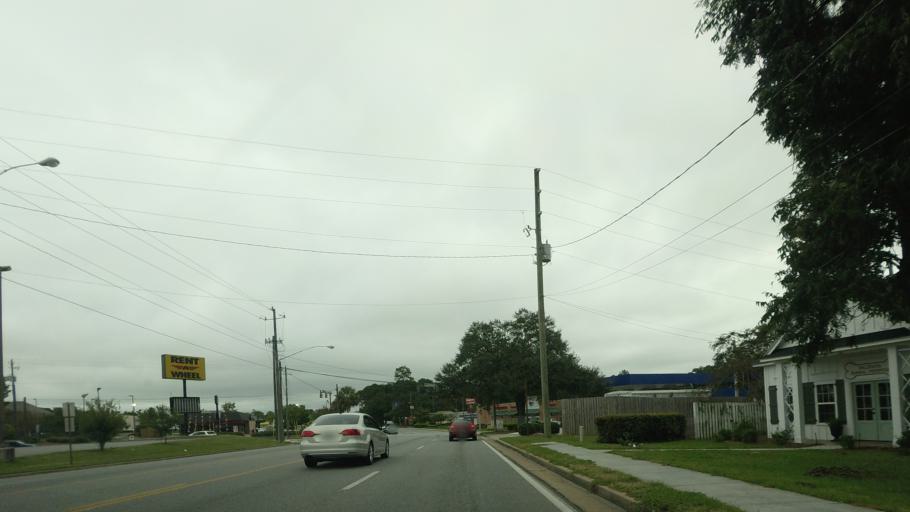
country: US
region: Georgia
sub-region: Lowndes County
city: Remerton
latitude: 30.8693
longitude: -83.2889
